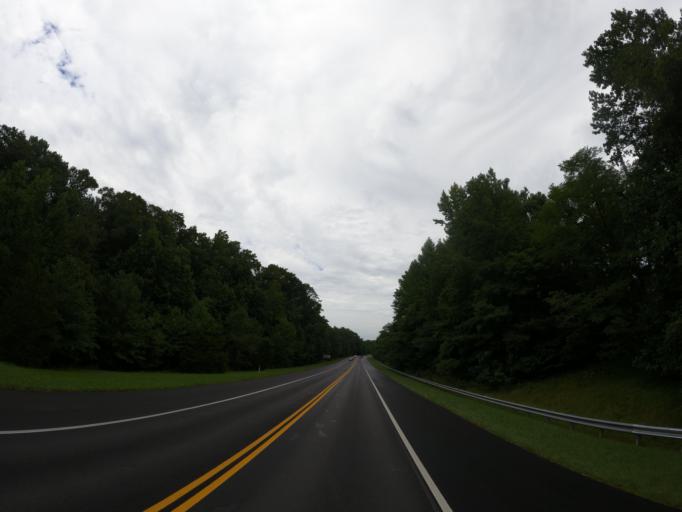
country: US
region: Maryland
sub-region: Saint Mary's County
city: California
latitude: 38.3132
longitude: -76.4940
